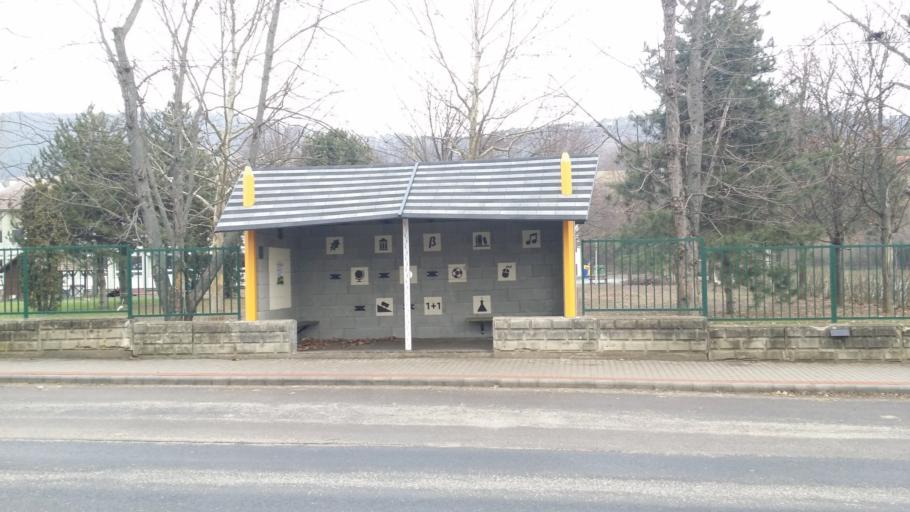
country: HU
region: Pest
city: Pilisborosjeno
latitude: 47.6022
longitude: 19.0022
